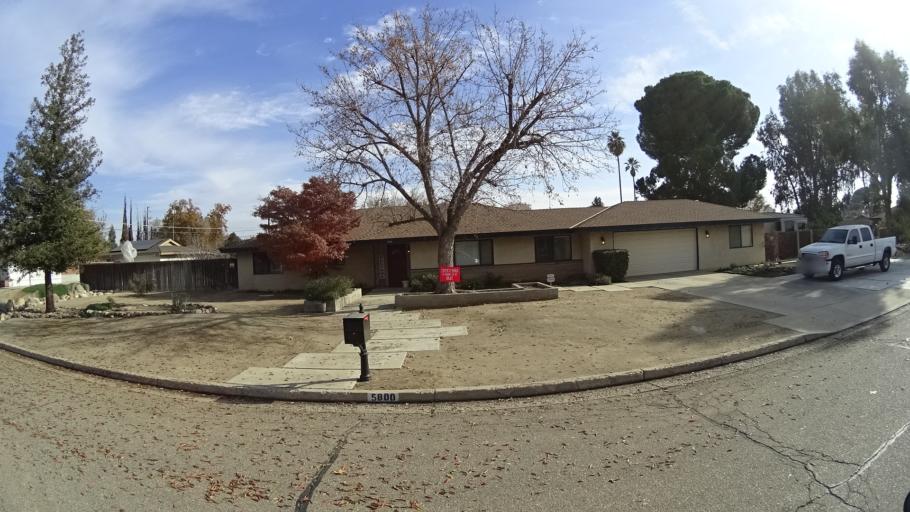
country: US
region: California
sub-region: Kern County
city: Oildale
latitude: 35.4117
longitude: -119.0664
